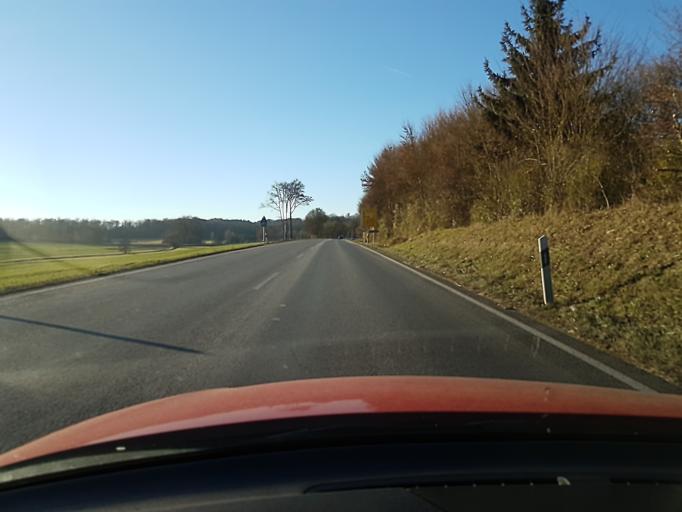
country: DE
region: Baden-Wuerttemberg
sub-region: Karlsruhe Region
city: Muhlacker
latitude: 48.9708
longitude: 8.8665
